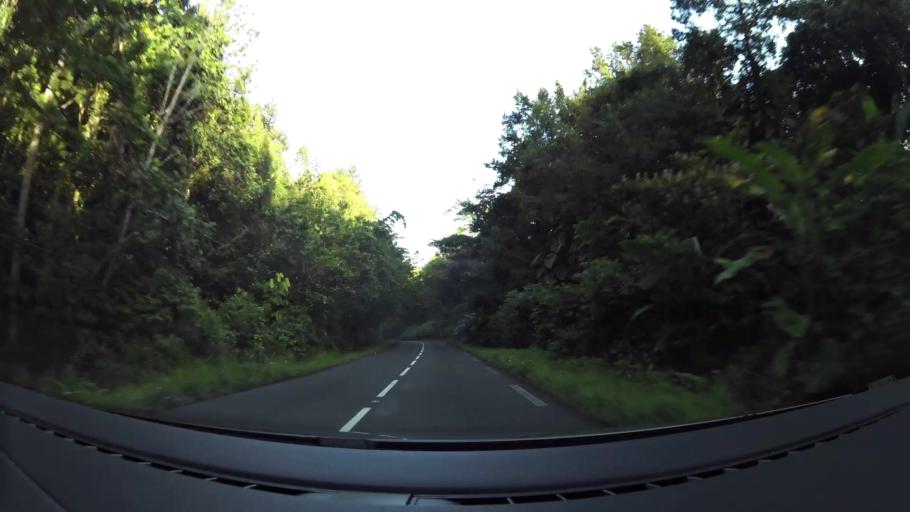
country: GP
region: Guadeloupe
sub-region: Guadeloupe
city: Bouillante
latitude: 16.1761
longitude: -61.7017
